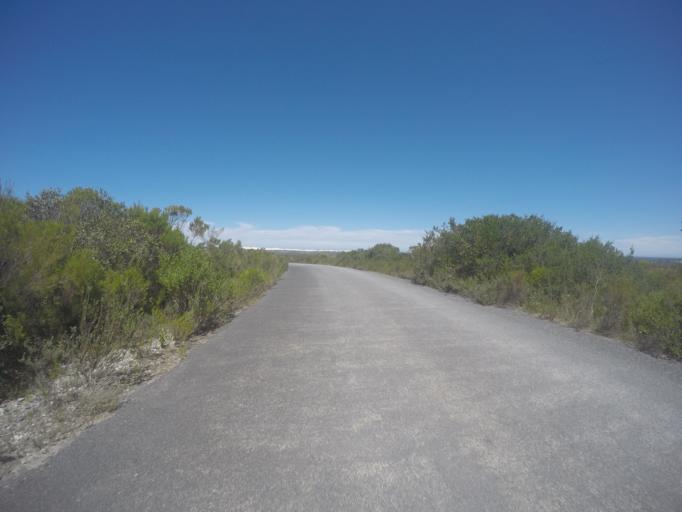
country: ZA
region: Western Cape
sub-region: Overberg District Municipality
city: Bredasdorp
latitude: -34.4332
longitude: 20.4186
